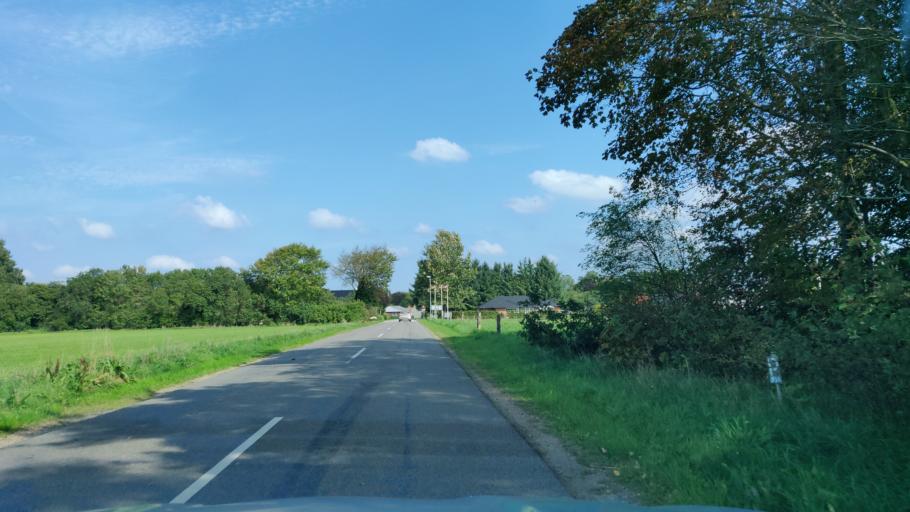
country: DK
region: Central Jutland
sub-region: Herning Kommune
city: Avlum
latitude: 56.2319
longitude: 8.8679
